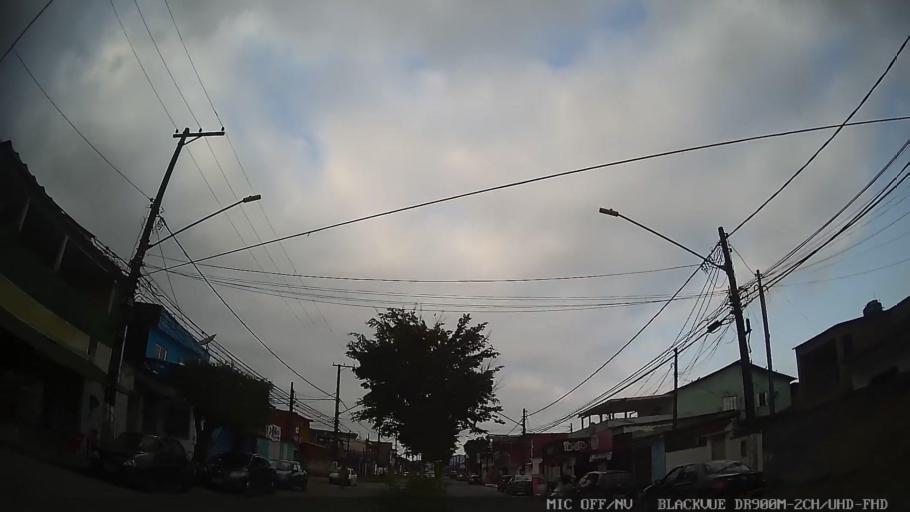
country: BR
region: Sao Paulo
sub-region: Santos
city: Santos
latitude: -23.9504
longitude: -46.2911
